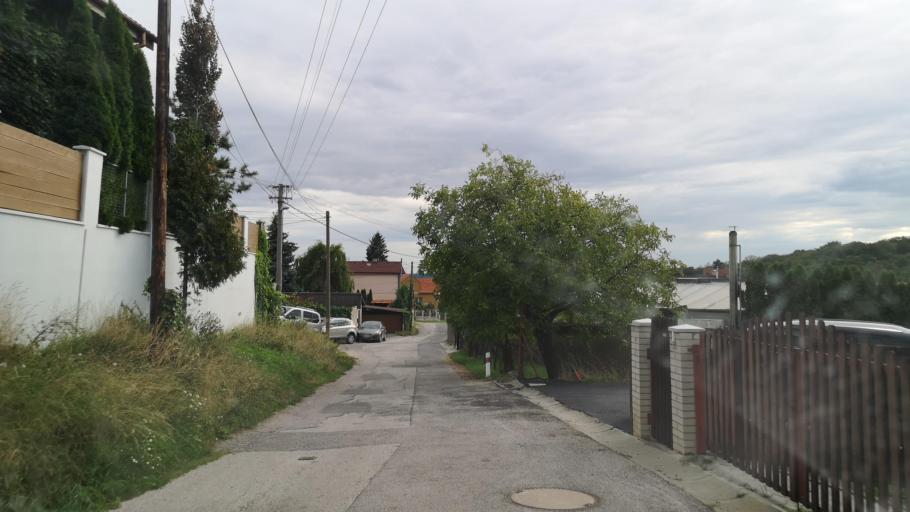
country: SK
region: Nitriansky
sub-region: Okres Nitra
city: Nitra
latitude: 48.3395
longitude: 18.0834
